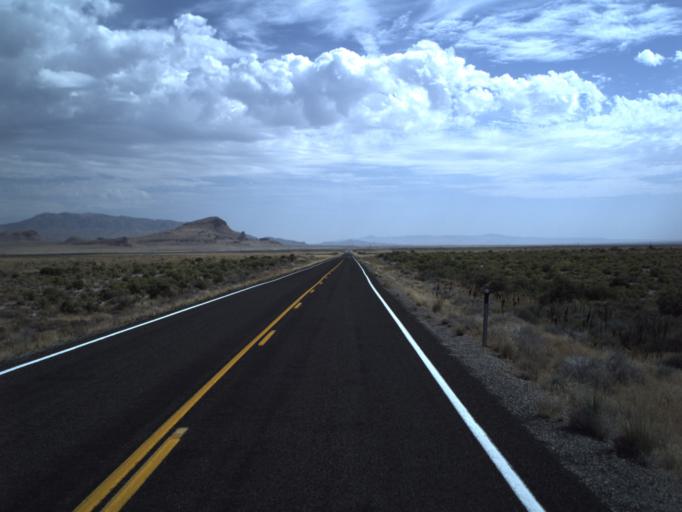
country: US
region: Utah
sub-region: Tooele County
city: Wendover
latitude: 41.4198
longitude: -113.9053
